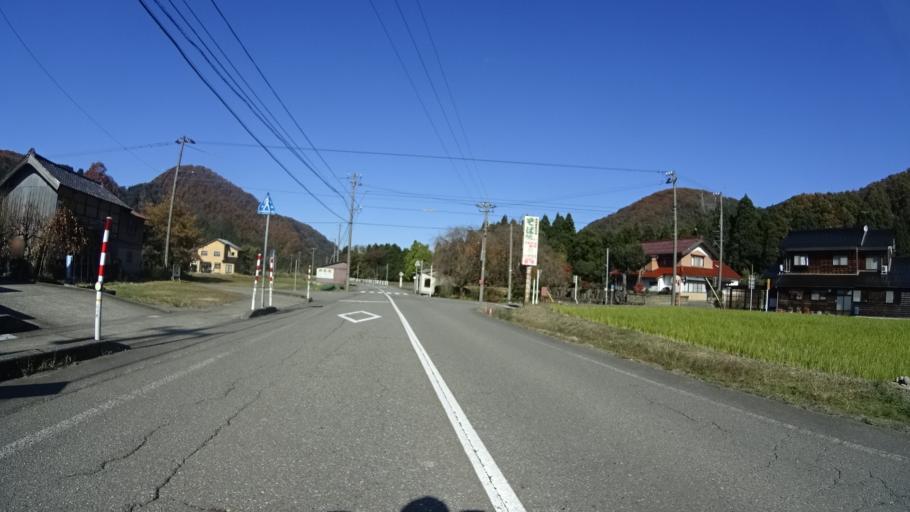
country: JP
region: Ishikawa
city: Tsurugi-asahimachi
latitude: 36.3431
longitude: 136.6305
